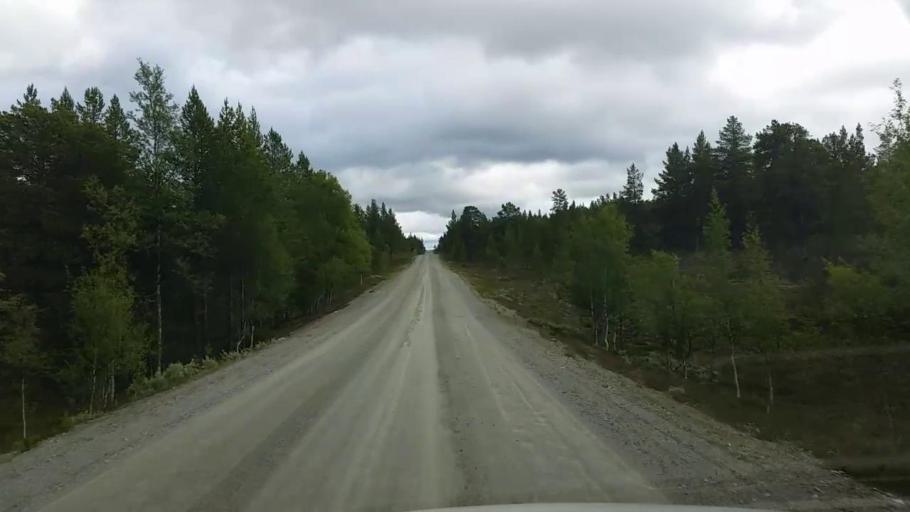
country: NO
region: Hedmark
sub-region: Engerdal
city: Engerdal
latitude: 62.3384
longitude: 12.6202
